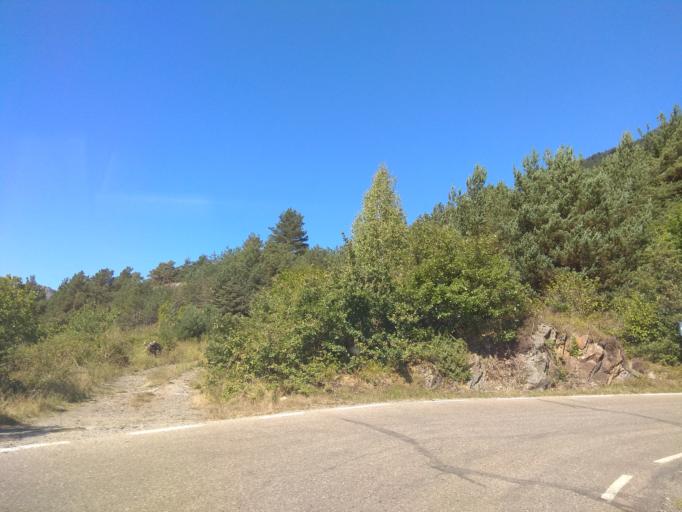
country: ES
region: Catalonia
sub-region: Provincia de Lleida
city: Vielha
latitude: 42.7430
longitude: 0.7408
